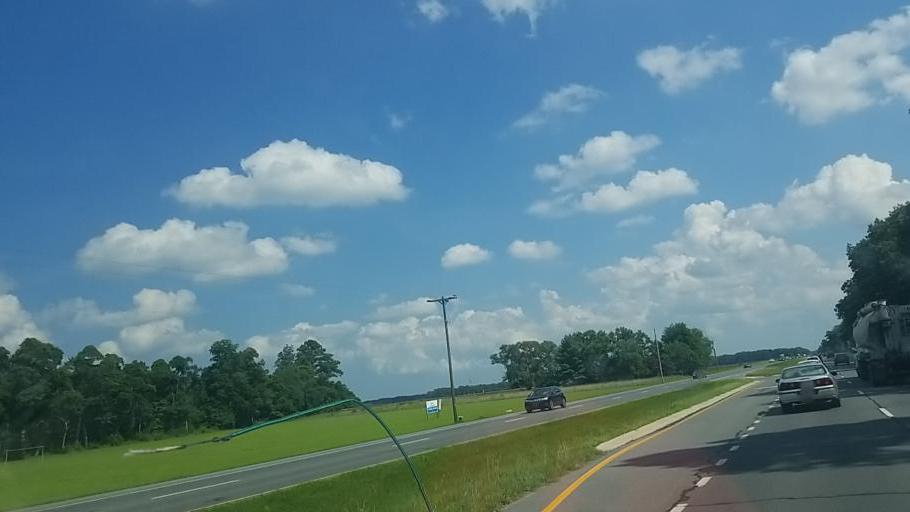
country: US
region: Delaware
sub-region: Sussex County
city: Millsboro
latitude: 38.6288
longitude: -75.3454
